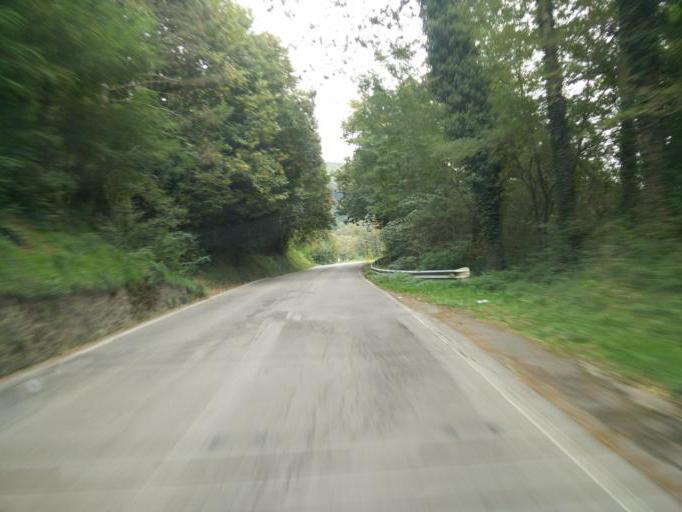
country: IT
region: Tuscany
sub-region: Provincia di Lucca
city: Camporgiano
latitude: 44.1729
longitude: 10.3302
